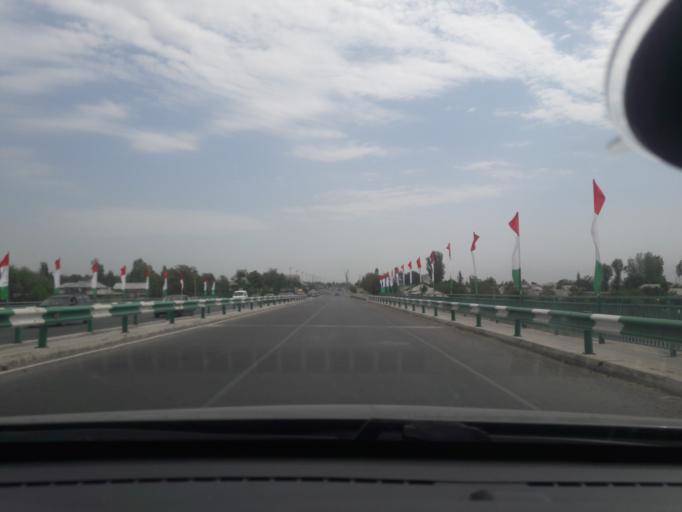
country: TJ
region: Republican Subordination
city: Hisor
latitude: 38.5560
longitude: 68.5501
